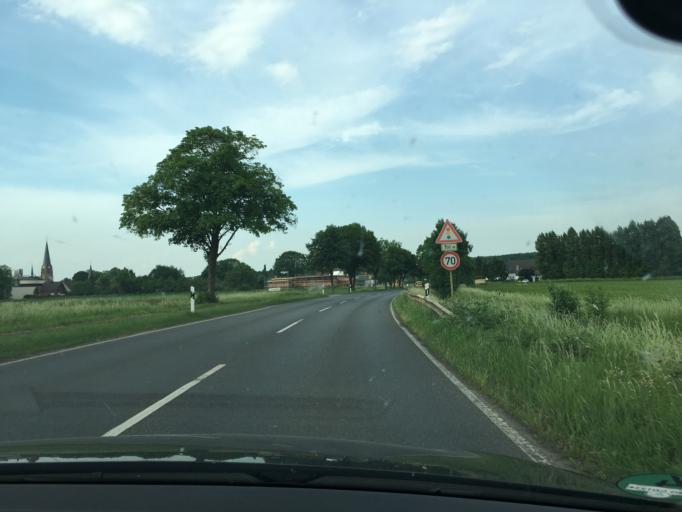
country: DE
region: North Rhine-Westphalia
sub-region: Regierungsbezirk Koln
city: Kreuzau
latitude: 50.7600
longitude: 6.4912
